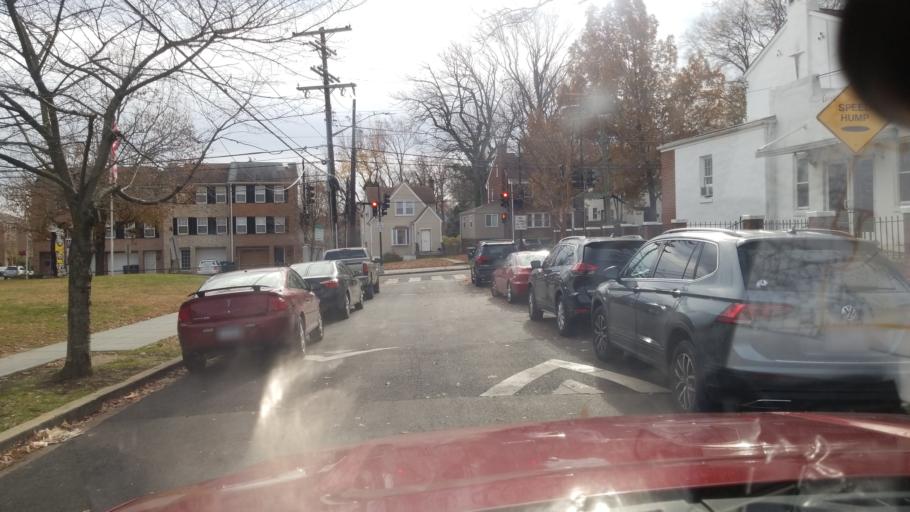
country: US
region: Maryland
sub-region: Prince George's County
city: Silver Hill
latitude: 38.8643
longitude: -76.9560
